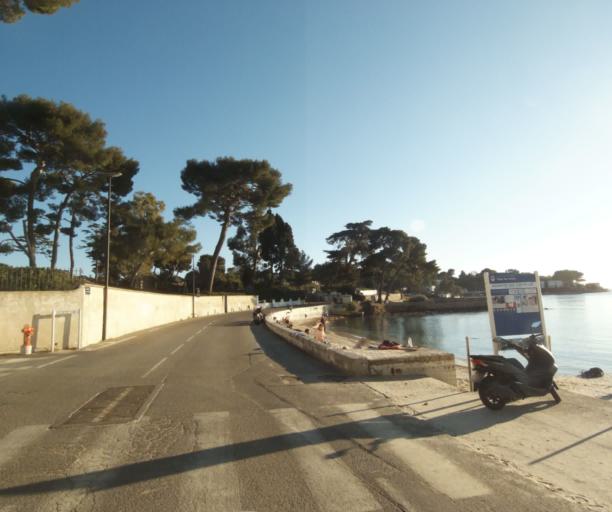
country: FR
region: Provence-Alpes-Cote d'Azur
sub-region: Departement des Alpes-Maritimes
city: Antibes
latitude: 43.5546
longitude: 7.1224
